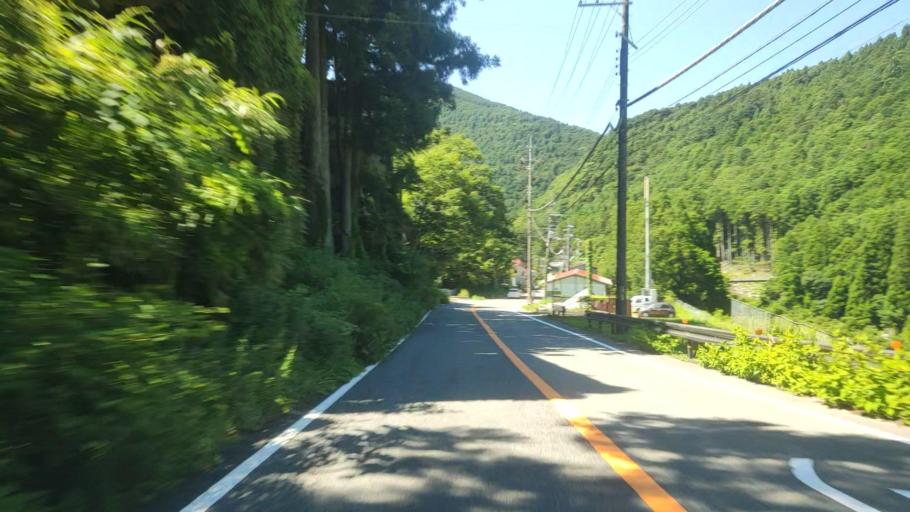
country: JP
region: Nara
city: Yoshino-cho
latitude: 34.2865
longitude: 136.0032
